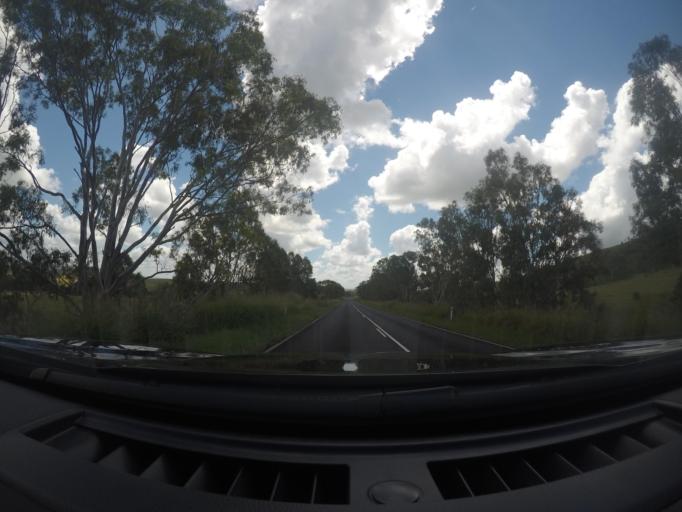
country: AU
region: Queensland
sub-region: Moreton Bay
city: Woodford
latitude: -27.1504
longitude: 152.5365
